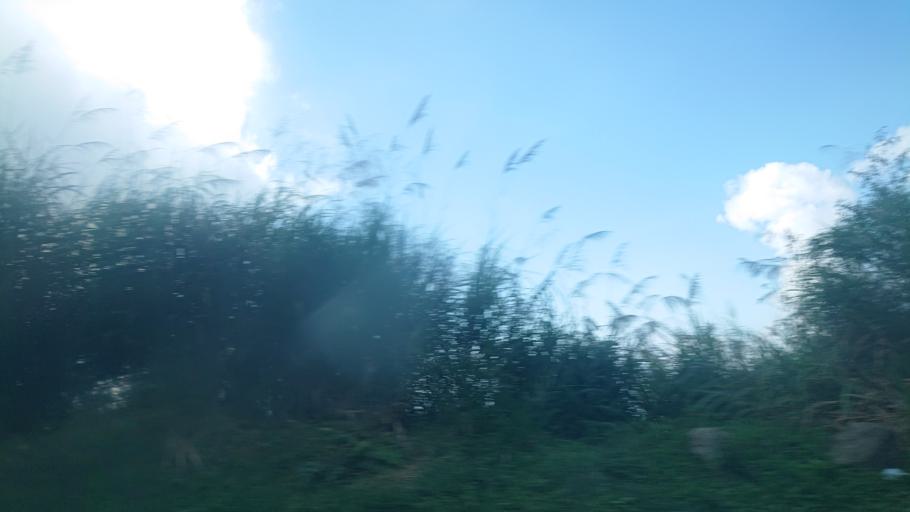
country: TW
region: Taiwan
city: Lugu
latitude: 23.5076
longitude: 120.7896
